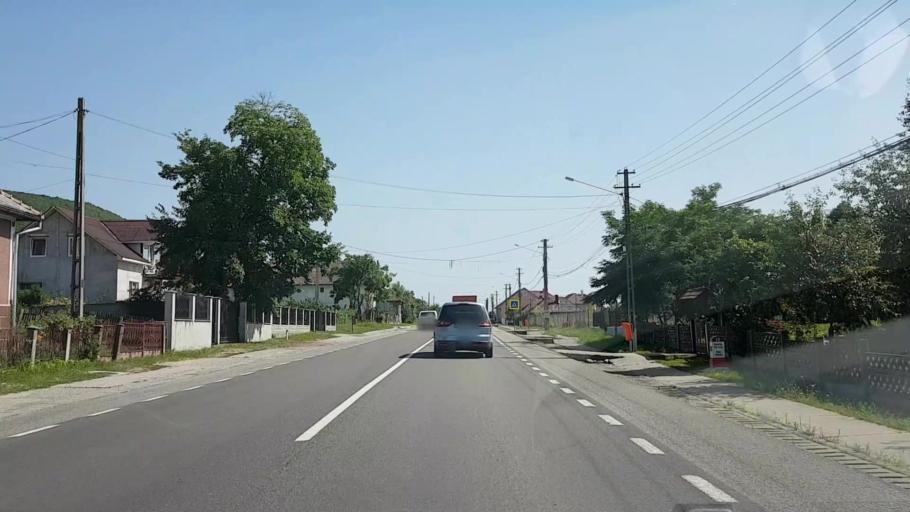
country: RO
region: Bistrita-Nasaud
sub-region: Comuna Sieu-Odorhei
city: Sieu-Odorhei
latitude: 47.1466
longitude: 24.3062
